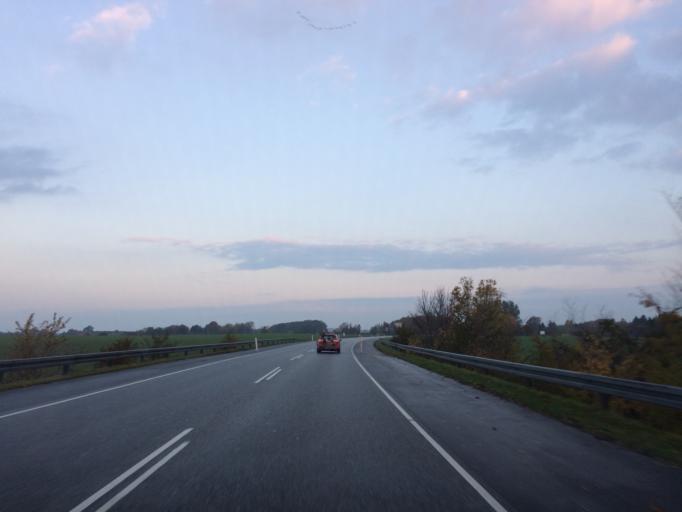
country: DK
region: Zealand
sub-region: Ringsted Kommune
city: Ringsted
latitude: 55.4730
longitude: 11.7415
